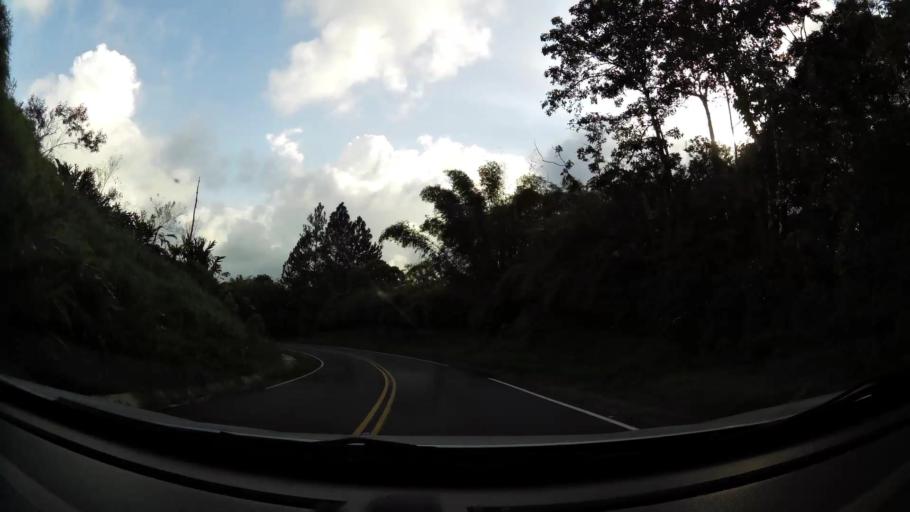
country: CR
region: Limon
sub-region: Canton de Siquirres
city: Siquirres
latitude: 10.0216
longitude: -83.5631
